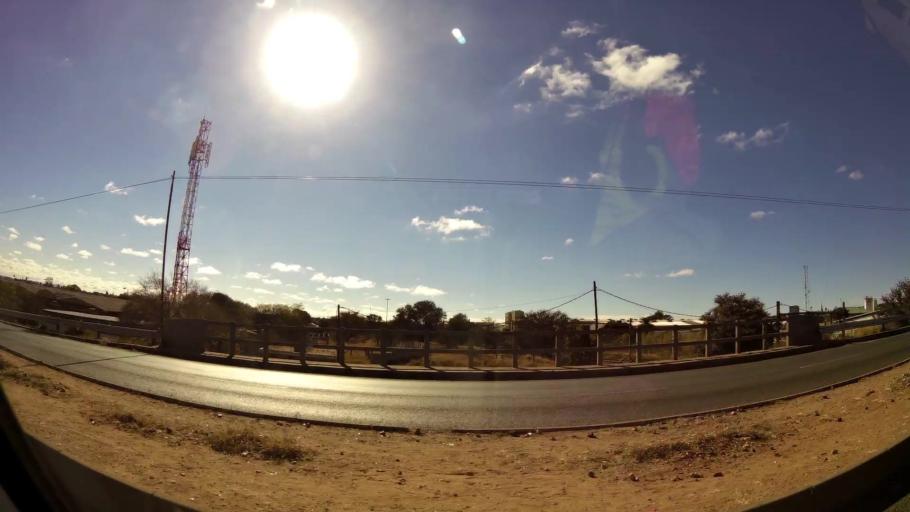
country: ZA
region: Limpopo
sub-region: Capricorn District Municipality
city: Polokwane
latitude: -23.8886
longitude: 29.4460
